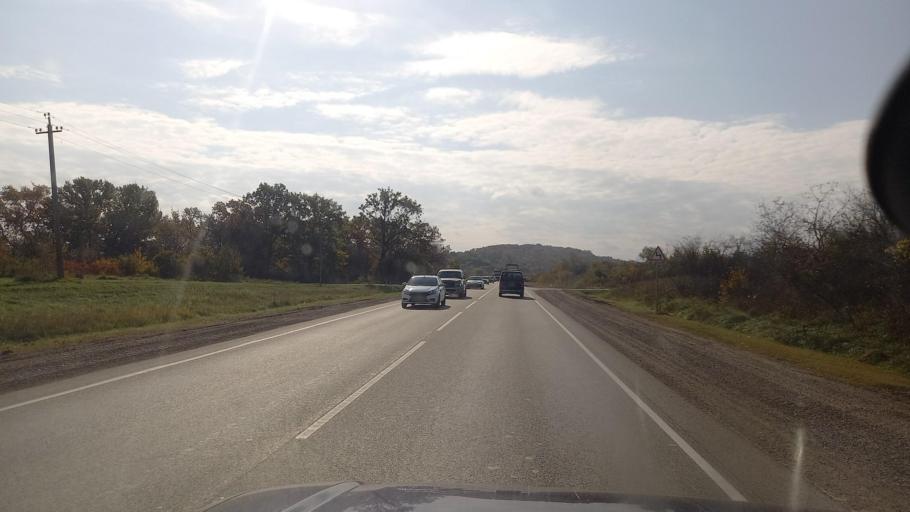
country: RU
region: Krasnodarskiy
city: Abinsk
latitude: 44.8555
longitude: 38.1336
